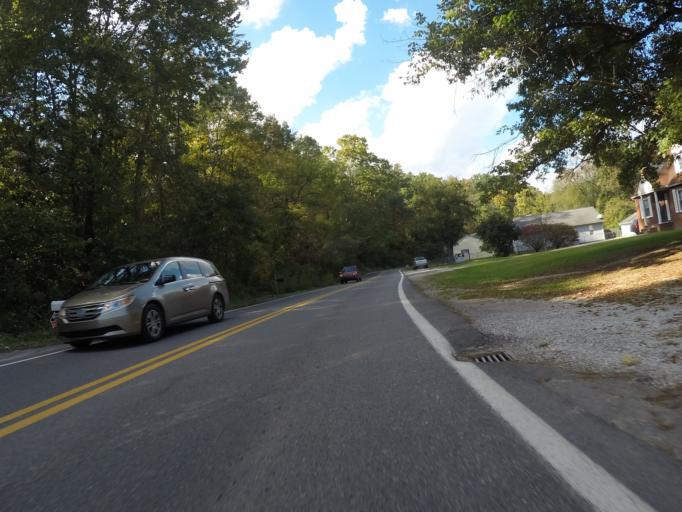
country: US
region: Ohio
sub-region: Lawrence County
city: Burlington
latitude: 38.3884
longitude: -82.5115
